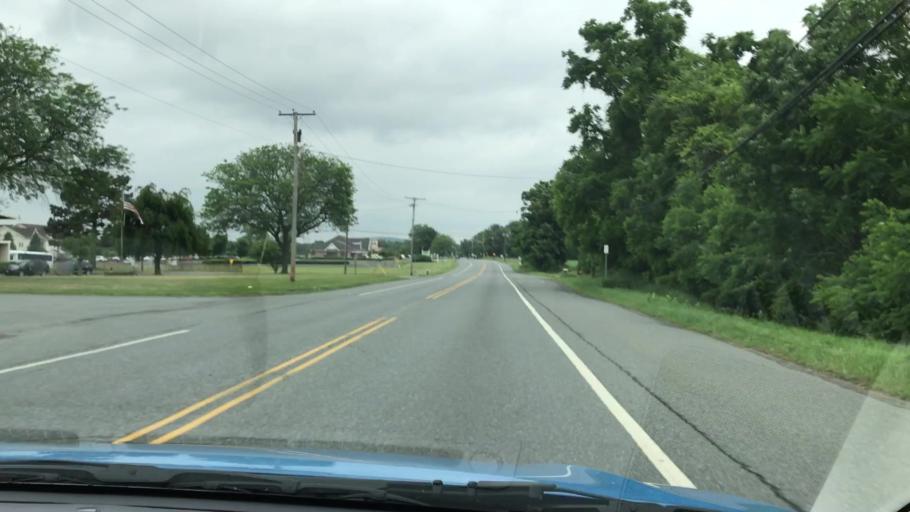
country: US
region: New Jersey
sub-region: Warren County
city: Belvidere
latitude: 40.8019
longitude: -75.0786
